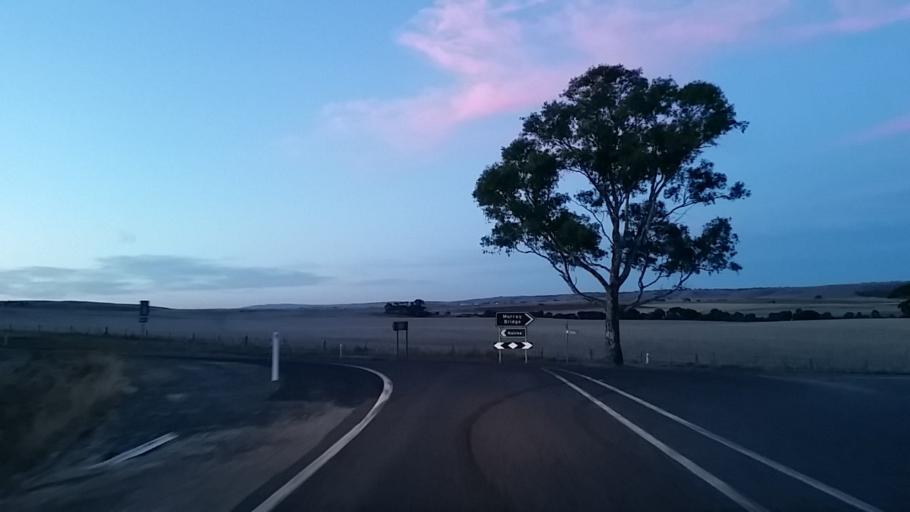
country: AU
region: South Australia
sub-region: Mount Barker
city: Callington
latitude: -35.1077
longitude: 139.0375
